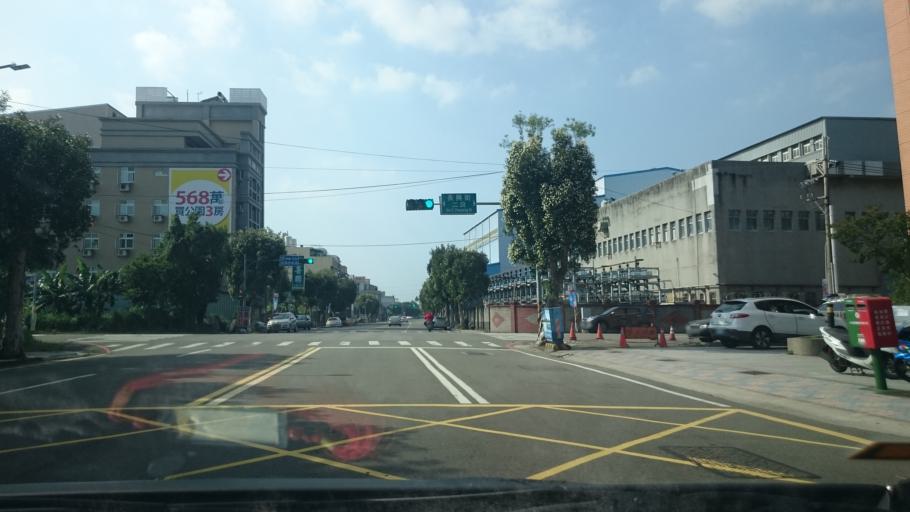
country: TW
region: Taiwan
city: Daxi
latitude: 24.9049
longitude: 121.2836
